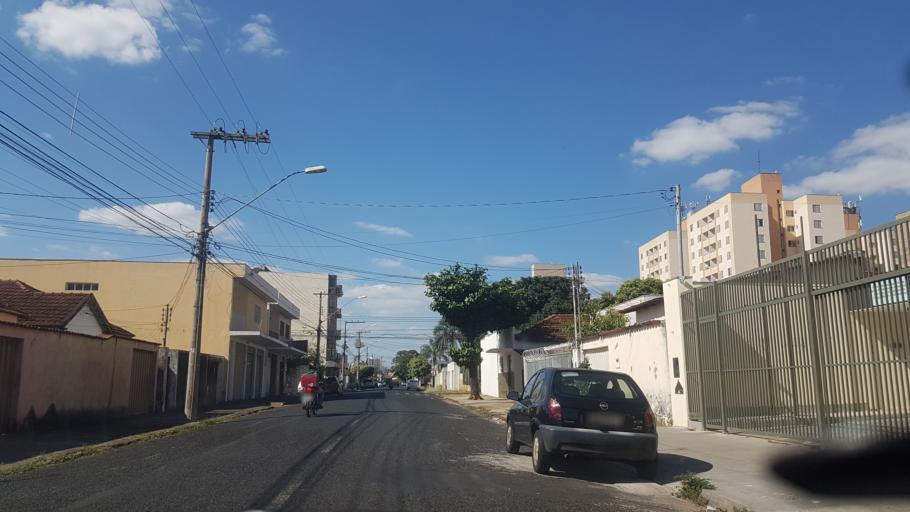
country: BR
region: Minas Gerais
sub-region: Uberlandia
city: Uberlandia
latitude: -18.9073
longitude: -48.2803
